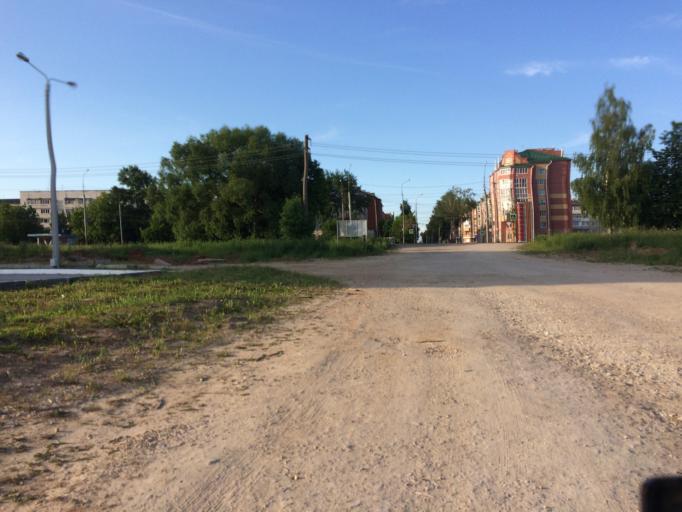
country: RU
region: Mariy-El
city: Medvedevo
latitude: 56.6402
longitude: 47.8024
